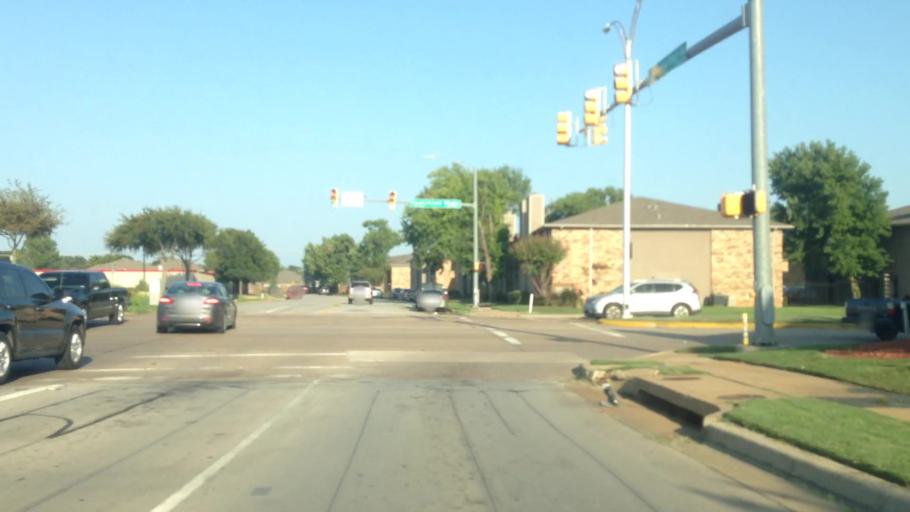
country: US
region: Texas
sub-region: Tarrant County
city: Pantego
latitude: 32.7520
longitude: -97.1720
